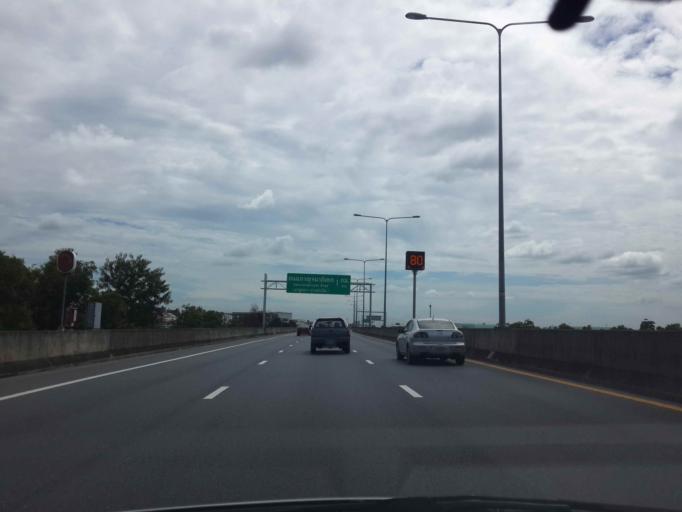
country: TH
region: Bangkok
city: Sai Mai
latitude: 13.8952
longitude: 100.6647
